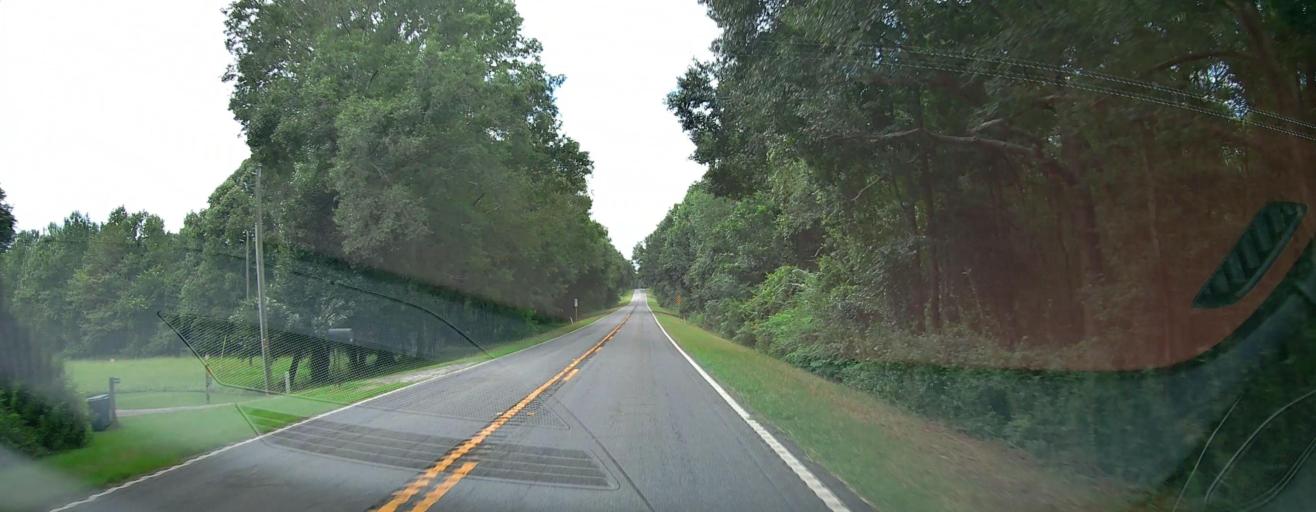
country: US
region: Georgia
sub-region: Dooly County
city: Unadilla
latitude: 32.2912
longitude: -83.8644
